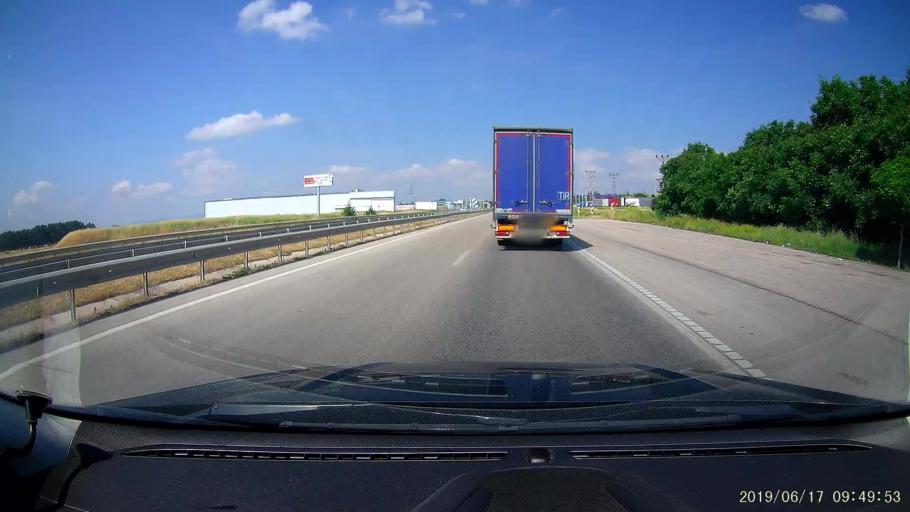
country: TR
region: Amasya
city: Merzifon
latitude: 40.8720
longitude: 35.5195
